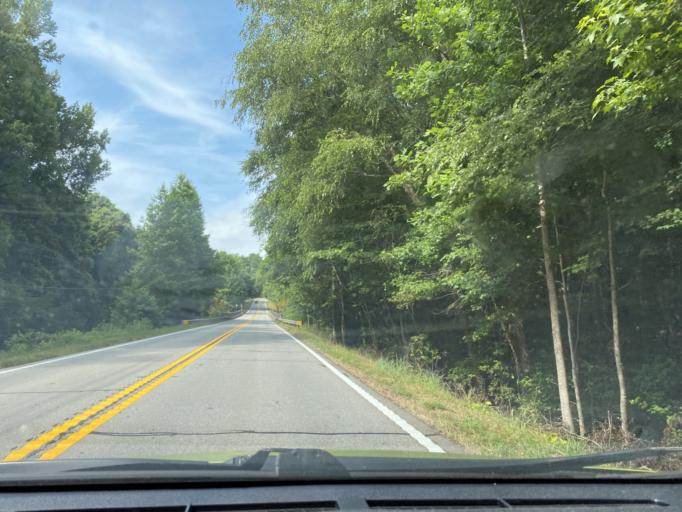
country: US
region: Georgia
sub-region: Coweta County
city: East Newnan
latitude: 33.2783
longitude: -84.7021
